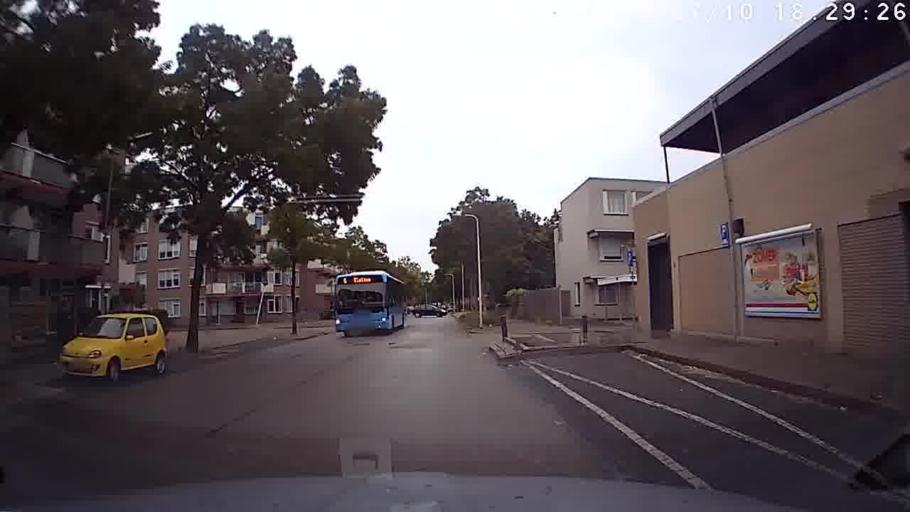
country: NL
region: Overijssel
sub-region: Gemeente Zwolle
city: Zwolle
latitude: 52.4839
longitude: 6.1139
